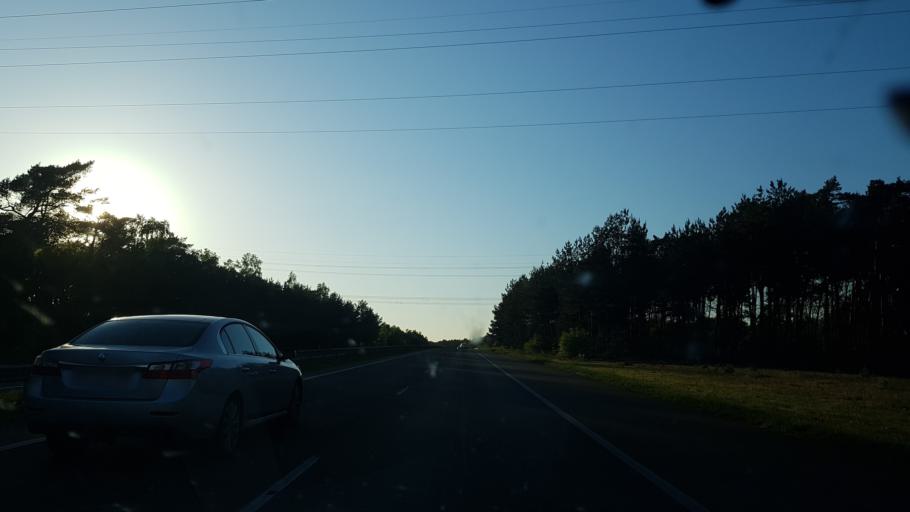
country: NL
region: Limburg
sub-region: Gemeente Leudal
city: Heythuysen
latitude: 51.2073
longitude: 5.9182
